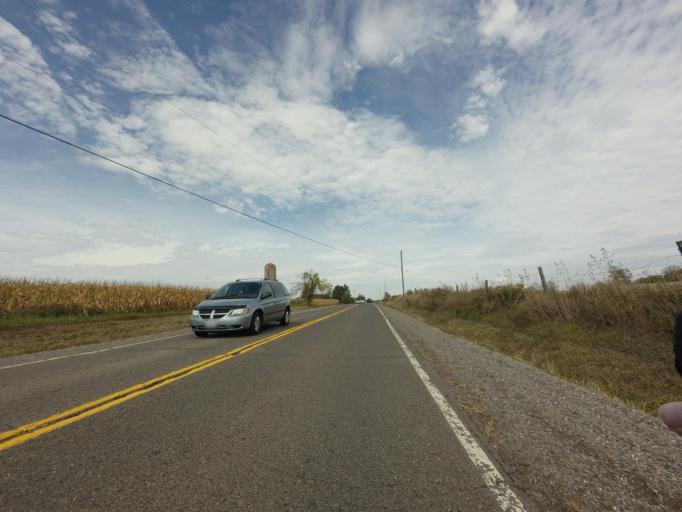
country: CA
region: Ontario
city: Ancaster
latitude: 43.2845
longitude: -79.9500
